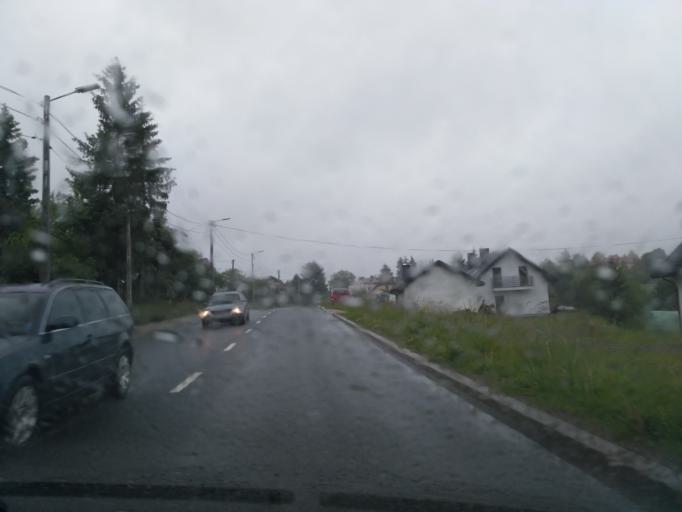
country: PL
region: Lesser Poland Voivodeship
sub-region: Powiat gorlicki
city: Gorlice
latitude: 49.6777
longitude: 21.1610
